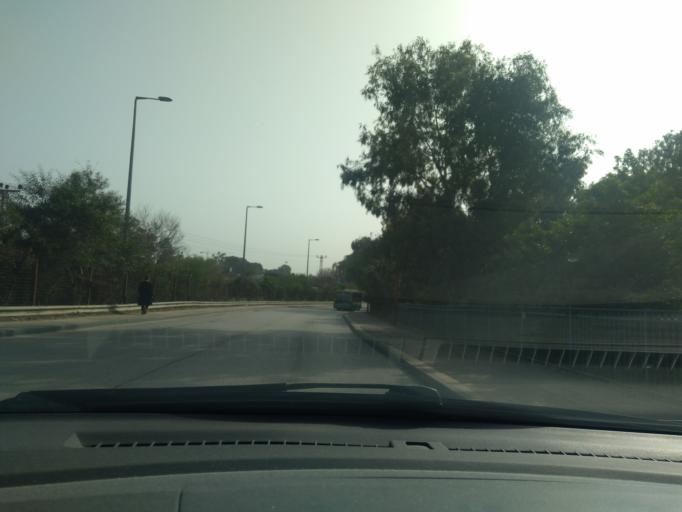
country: IL
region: Central District
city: Netanya
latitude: 32.3240
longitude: 34.8690
